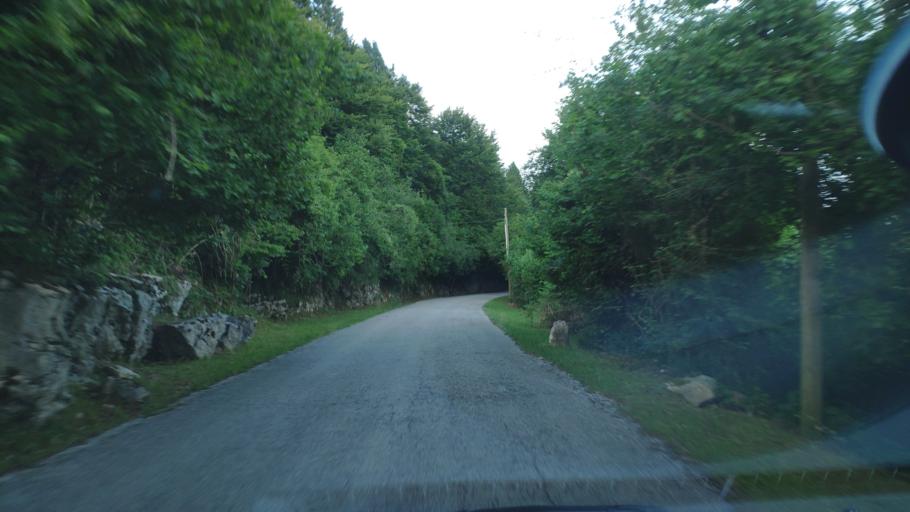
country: IT
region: Veneto
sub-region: Provincia di Vicenza
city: Calvene
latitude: 45.7919
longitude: 11.5078
